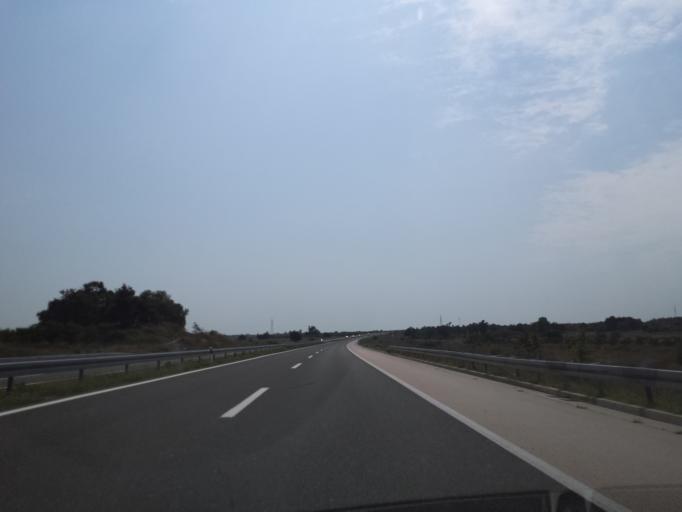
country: HR
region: Zadarska
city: Policnik
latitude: 44.1552
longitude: 15.4202
